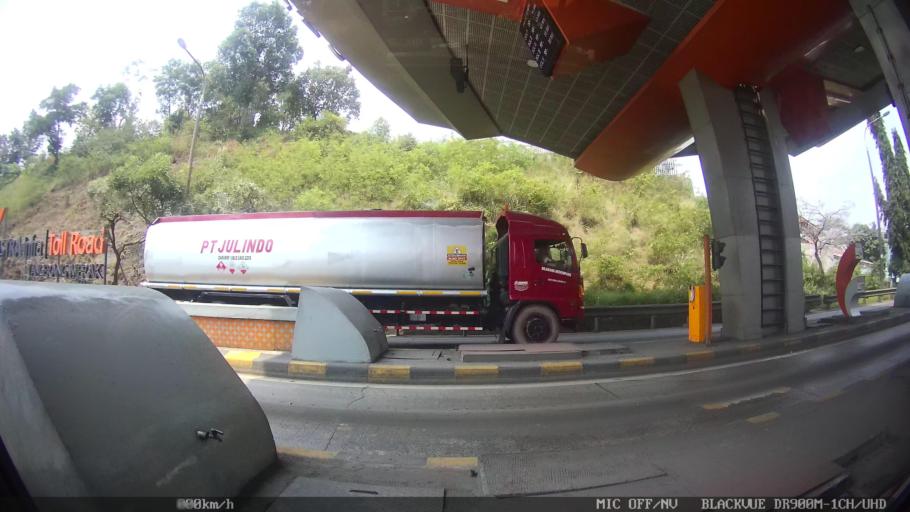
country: ID
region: Banten
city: Curug
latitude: -5.9732
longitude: 106.0088
